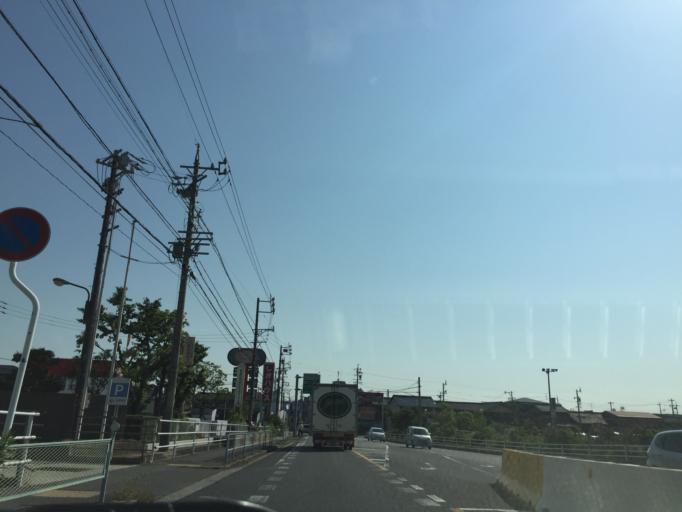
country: JP
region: Mie
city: Yokkaichi
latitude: 35.0093
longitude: 136.6558
